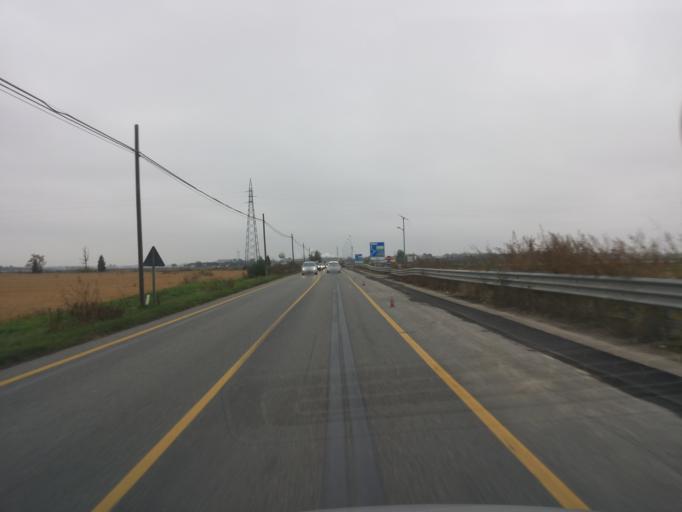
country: IT
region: Piedmont
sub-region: Provincia di Novara
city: Lumellogno
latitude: 45.4159
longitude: 8.5668
